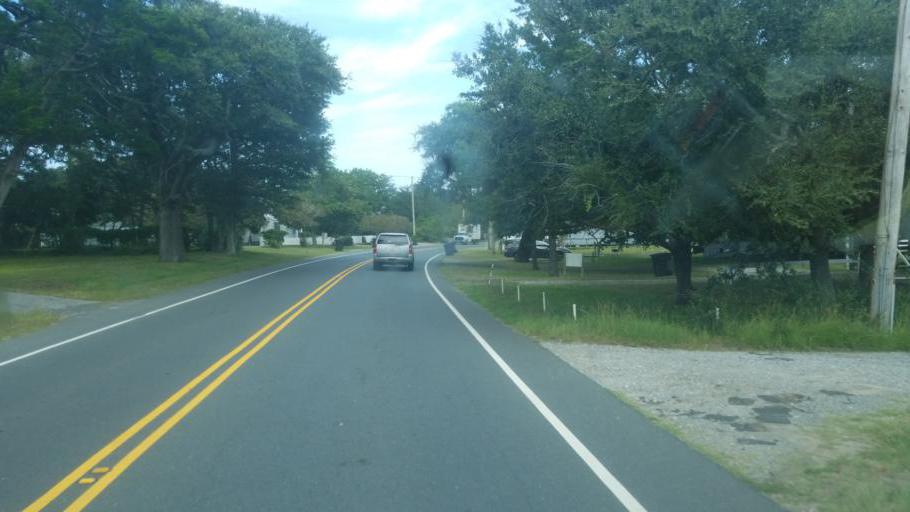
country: US
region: North Carolina
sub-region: Dare County
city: Buxton
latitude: 35.2691
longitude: -75.5361
